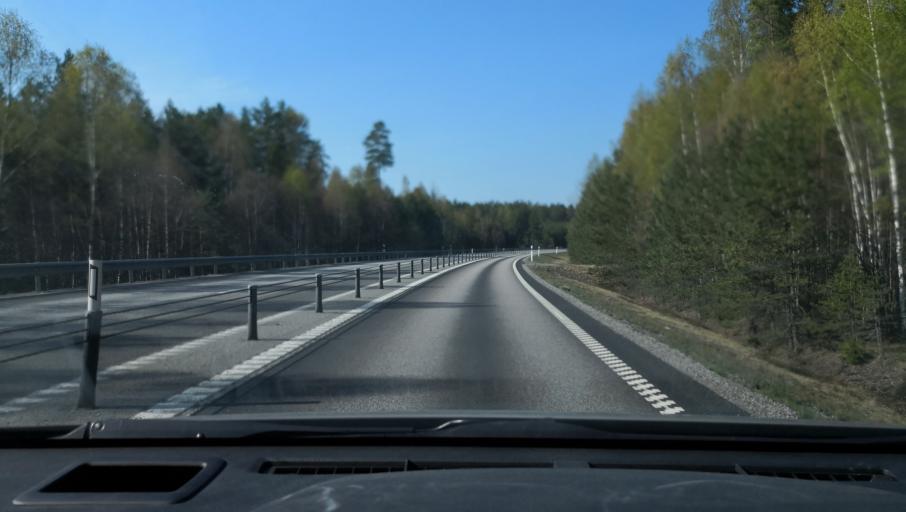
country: SE
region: Uppsala
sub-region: Heby Kommun
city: Tarnsjo
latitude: 60.1798
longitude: 16.9465
